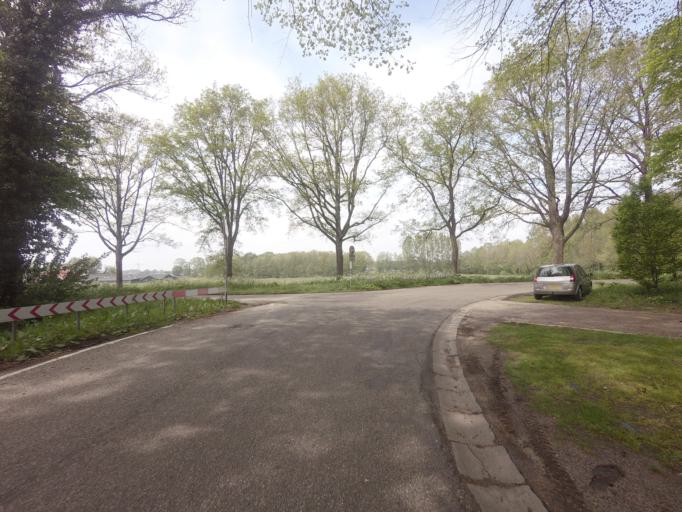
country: NL
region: Overijssel
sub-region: Gemeente Hof van Twente
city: Delden
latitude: 52.2465
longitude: 6.6768
